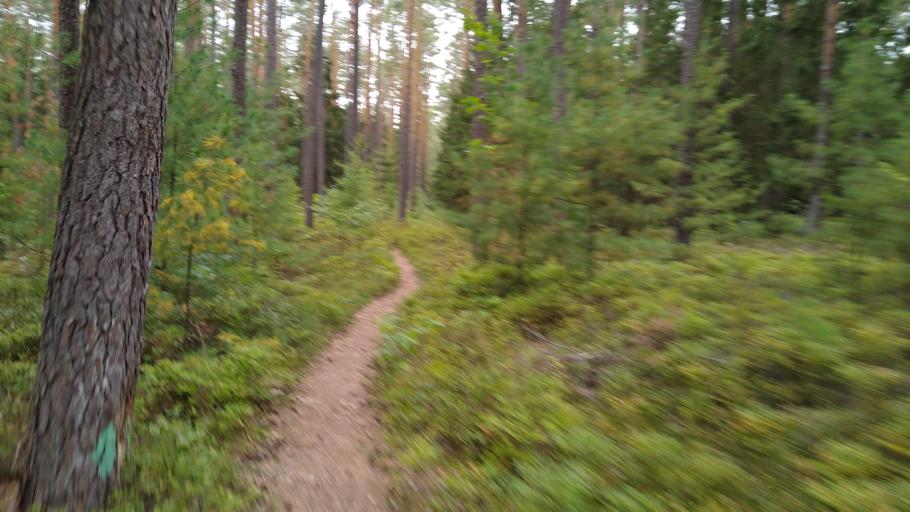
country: DE
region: Bavaria
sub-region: Regierungsbezirk Mittelfranken
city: Seukendorf
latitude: 49.4684
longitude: 10.9210
